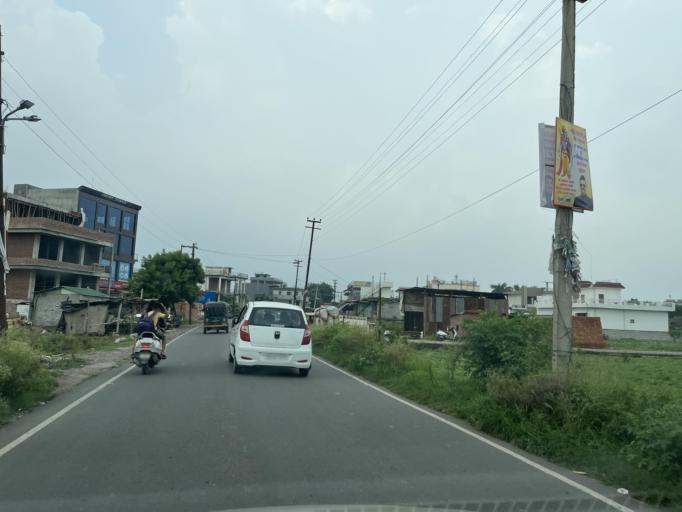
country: IN
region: Uttarakhand
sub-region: Naini Tal
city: Haldwani
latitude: 29.1980
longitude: 79.4860
